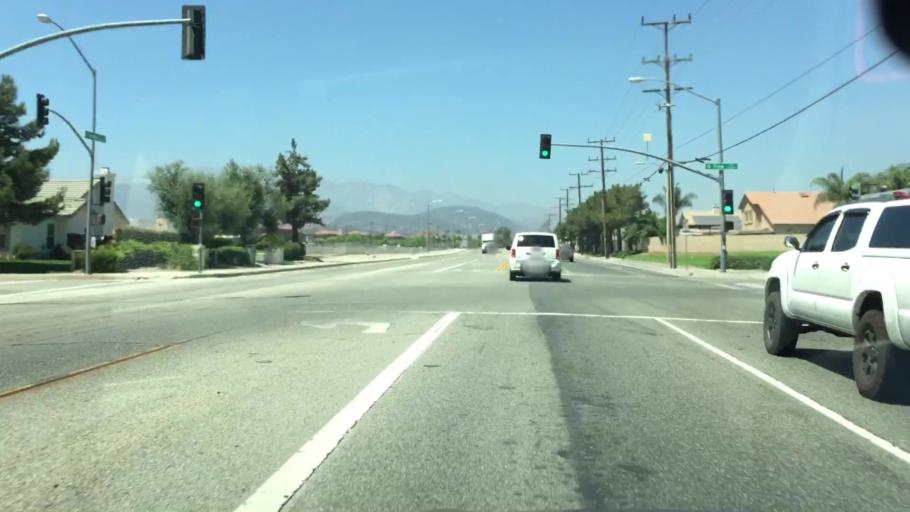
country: US
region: California
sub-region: San Bernardino County
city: Muscoy
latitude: 34.1865
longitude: -117.3510
